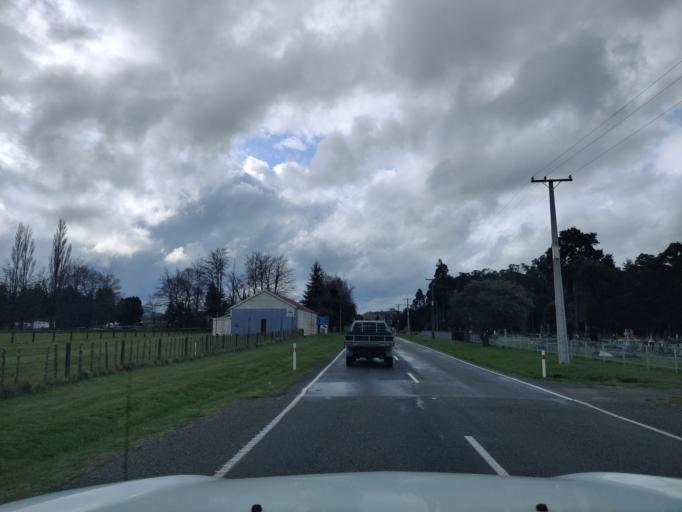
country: NZ
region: Manawatu-Wanganui
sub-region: Ruapehu District
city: Waiouru
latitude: -39.4348
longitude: 175.2835
